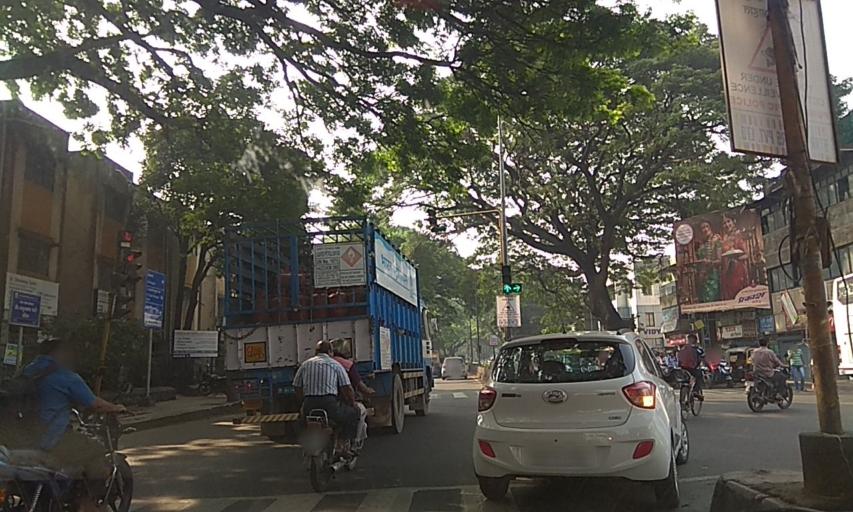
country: IN
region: Maharashtra
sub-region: Pune Division
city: Pune
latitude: 18.5052
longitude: 73.8449
